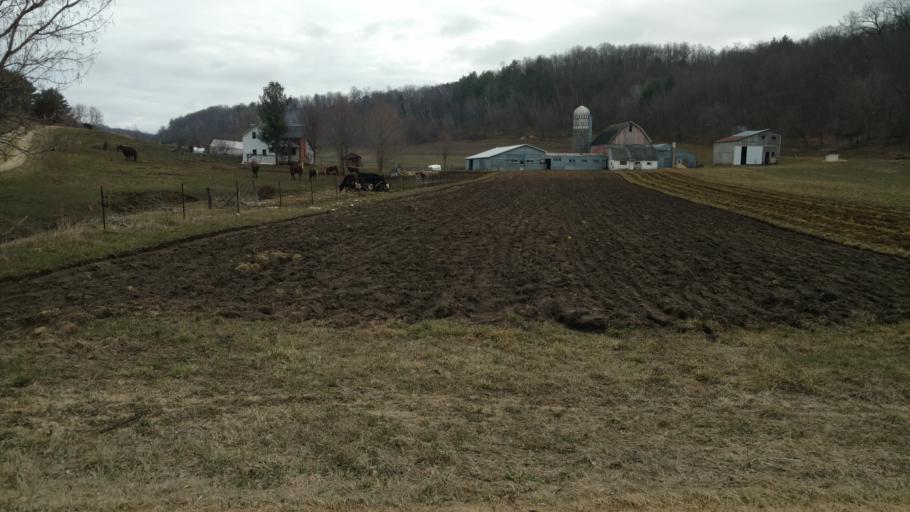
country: US
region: Wisconsin
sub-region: Vernon County
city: Hillsboro
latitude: 43.5835
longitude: -90.4069
